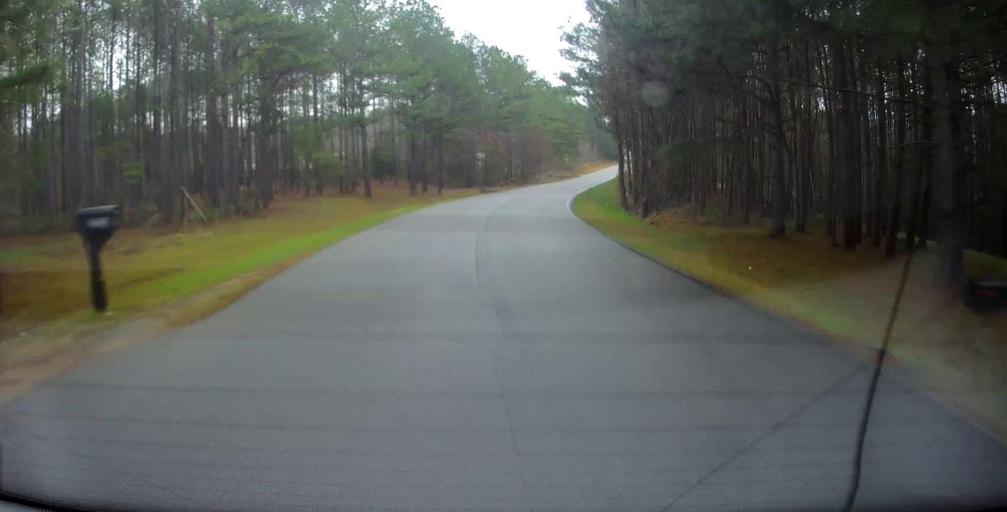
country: US
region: Georgia
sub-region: Monroe County
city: Forsyth
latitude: 33.0843
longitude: -83.9166
